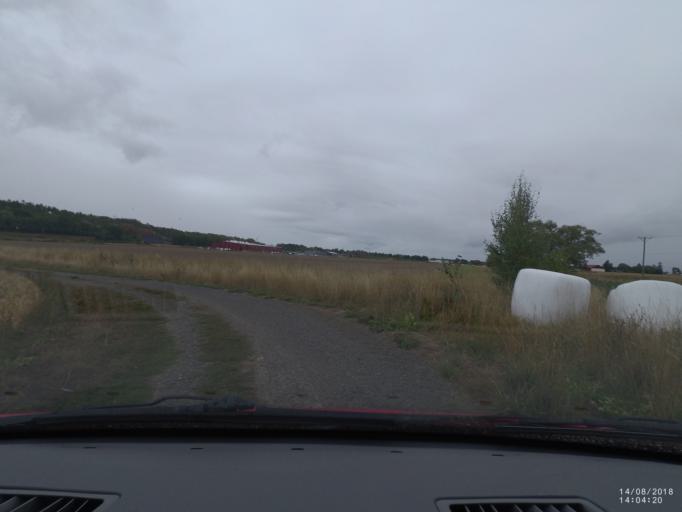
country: SE
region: Soedermanland
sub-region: Nykopings Kommun
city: Nykoping
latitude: 58.7550
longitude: 16.9623
